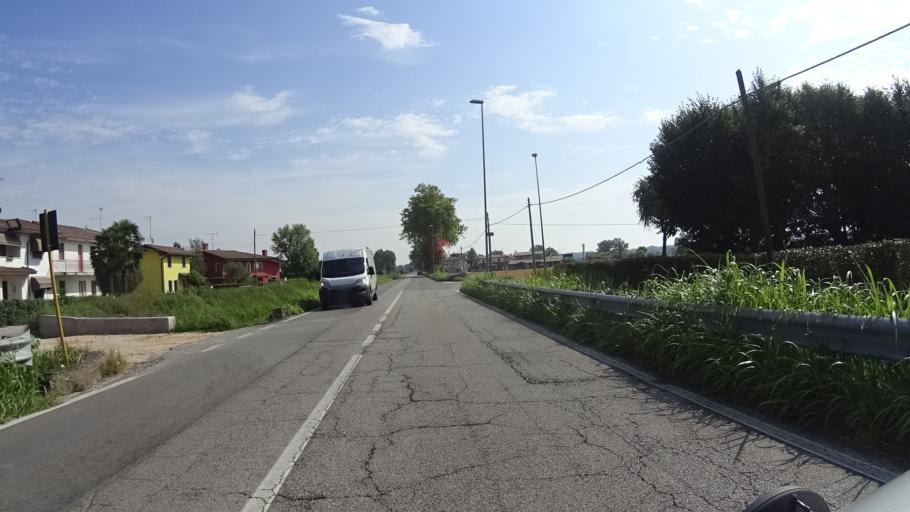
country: IT
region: Veneto
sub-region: Provincia di Venezia
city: Lugugnana
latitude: 45.7425
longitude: 12.9768
